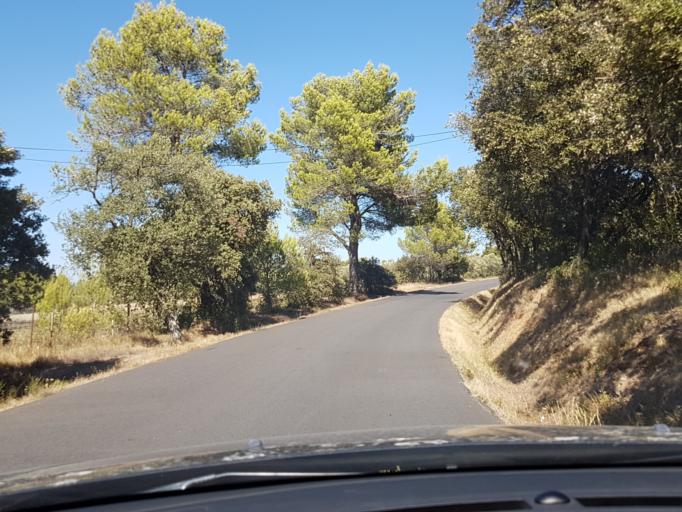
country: FR
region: Provence-Alpes-Cote d'Azur
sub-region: Departement des Bouches-du-Rhone
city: Orgon
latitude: 43.7815
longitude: 5.0124
